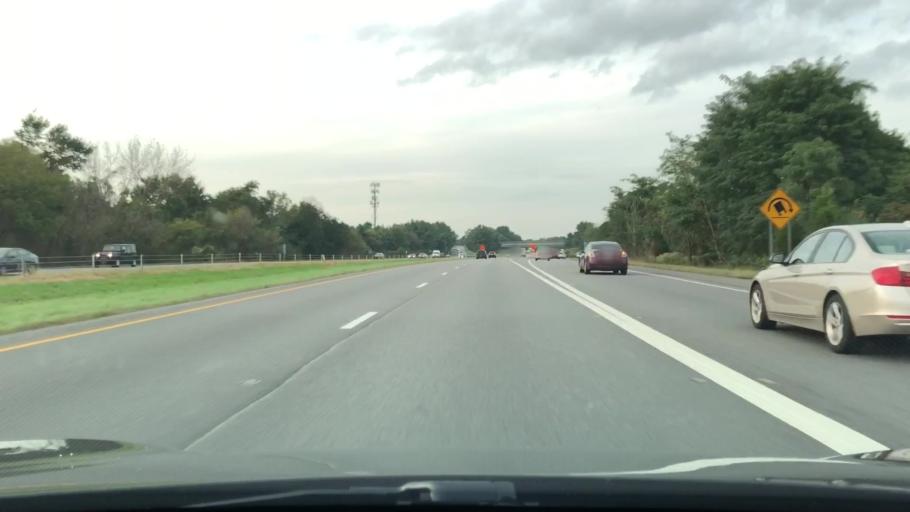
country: US
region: Pennsylvania
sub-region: Bucks County
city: Woodside
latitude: 40.2280
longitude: -74.8818
